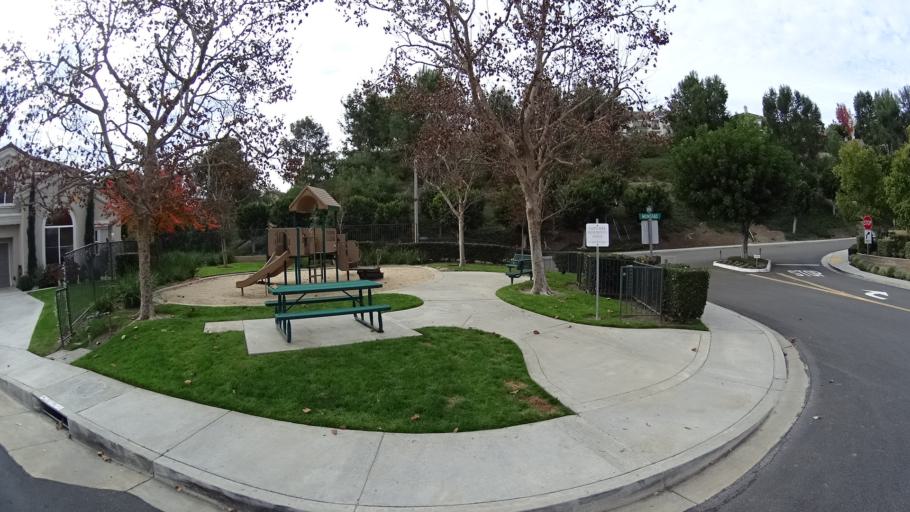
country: US
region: California
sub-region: Orange County
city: Aliso Viejo
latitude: 33.5545
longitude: -117.7286
